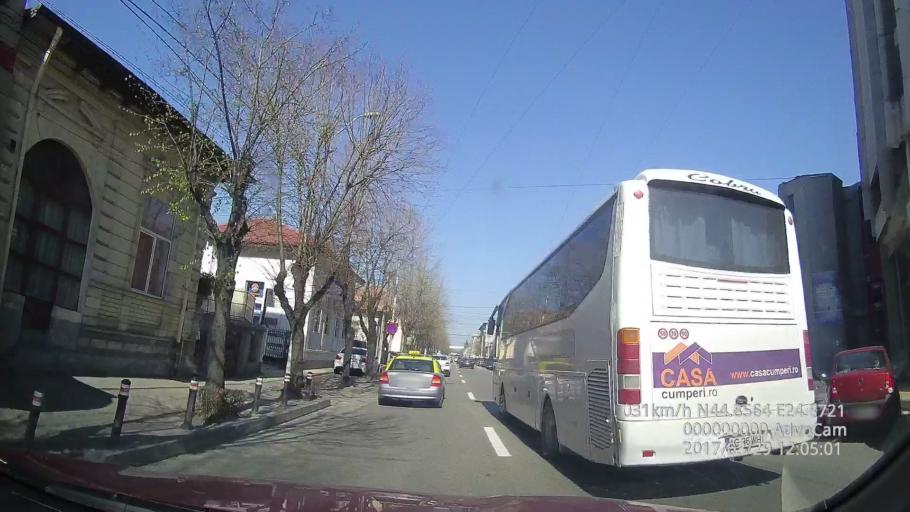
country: RO
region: Arges
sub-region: Comuna Albestii de Arges
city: Pitesti
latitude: 44.8565
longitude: 24.8719
